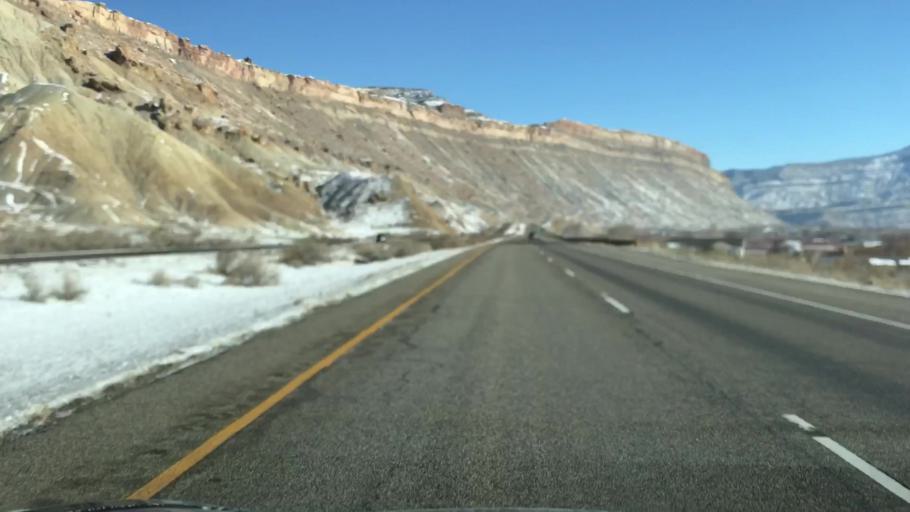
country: US
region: Colorado
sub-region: Mesa County
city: Palisade
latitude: 39.1173
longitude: -108.3906
